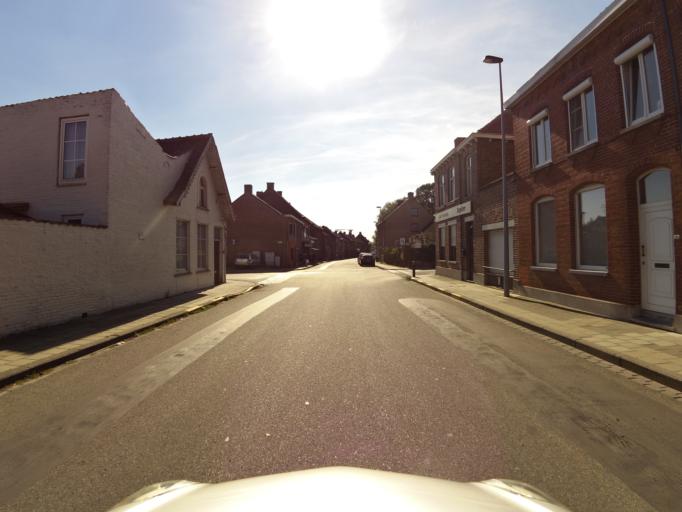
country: BE
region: Flanders
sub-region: Provincie West-Vlaanderen
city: Poperinge
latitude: 50.8606
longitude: 2.7311
